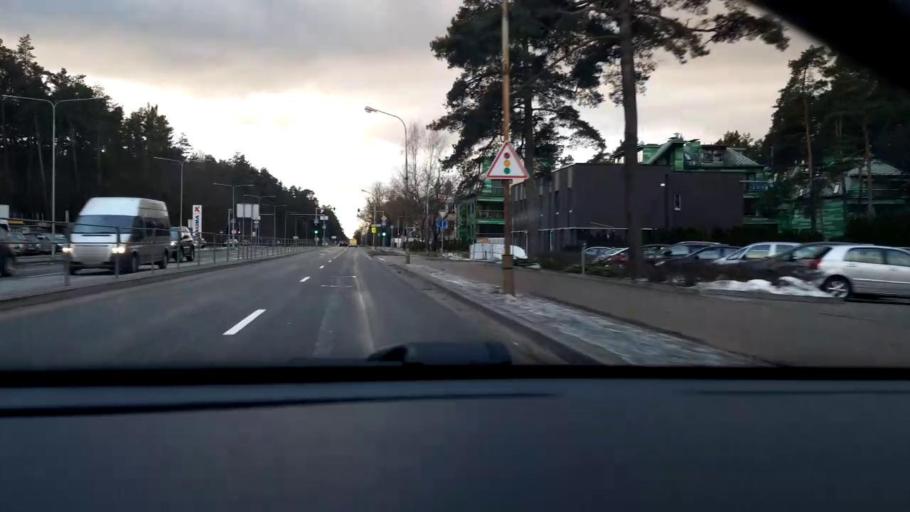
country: LT
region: Vilnius County
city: Rasos
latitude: 54.7352
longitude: 25.3389
